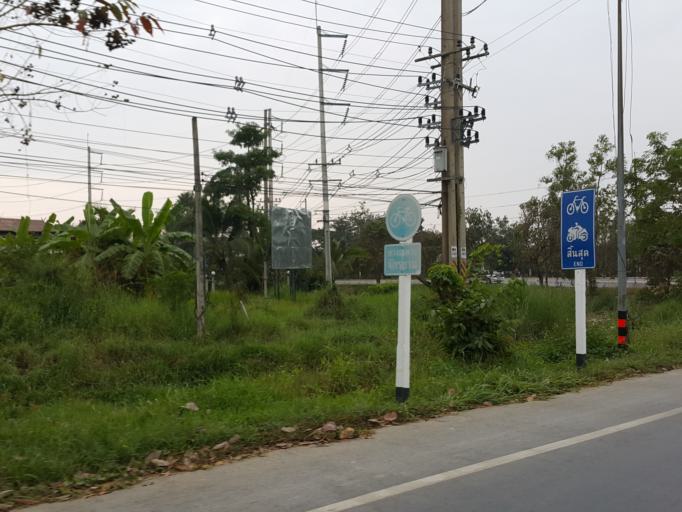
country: TH
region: Chiang Mai
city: Saraphi
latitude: 18.7485
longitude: 99.0688
